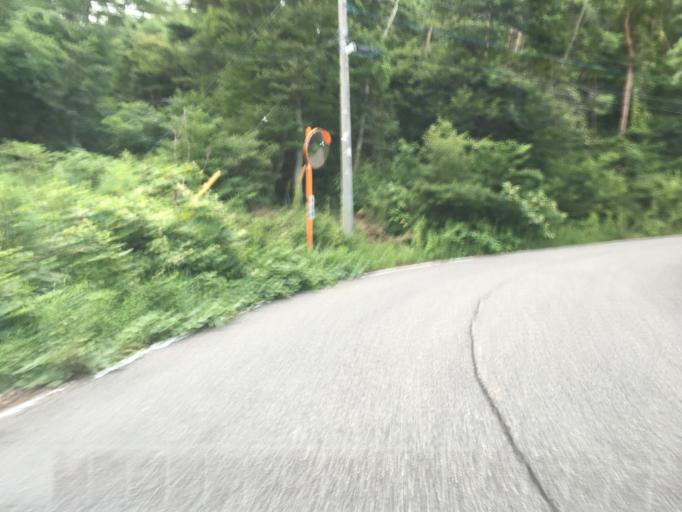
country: JP
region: Fukushima
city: Nihommatsu
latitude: 37.6188
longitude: 140.3392
